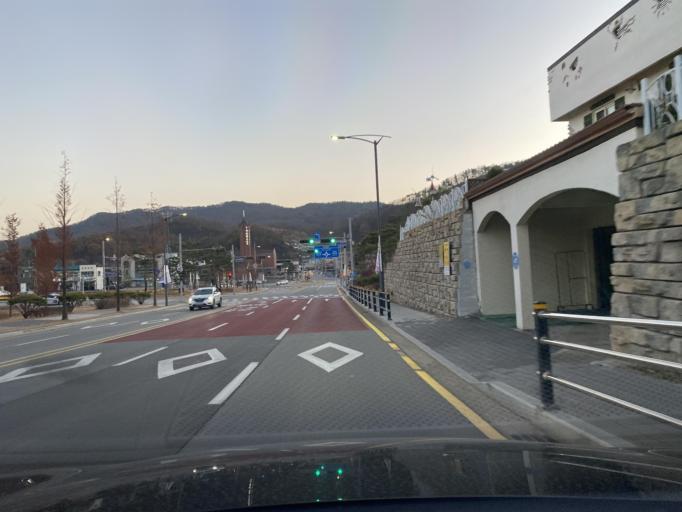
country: KR
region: Chungcheongnam-do
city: Yesan
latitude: 36.6801
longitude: 126.8434
